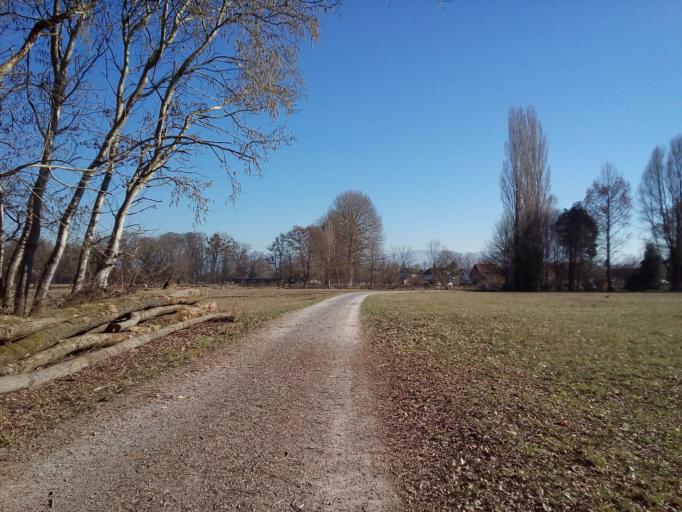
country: DE
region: Baden-Wuerttemberg
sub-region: Karlsruhe Region
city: Schwarzach
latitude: 48.7370
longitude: 8.0556
